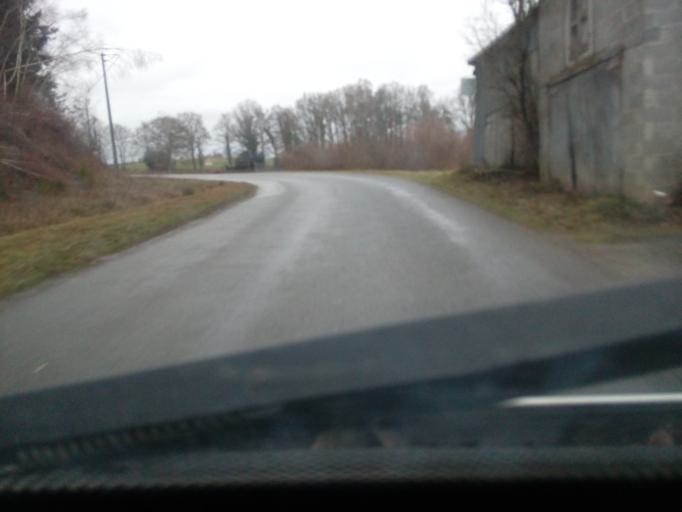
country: FR
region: Limousin
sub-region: Departement de la Creuse
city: Felletin
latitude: 45.8601
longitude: 2.2189
